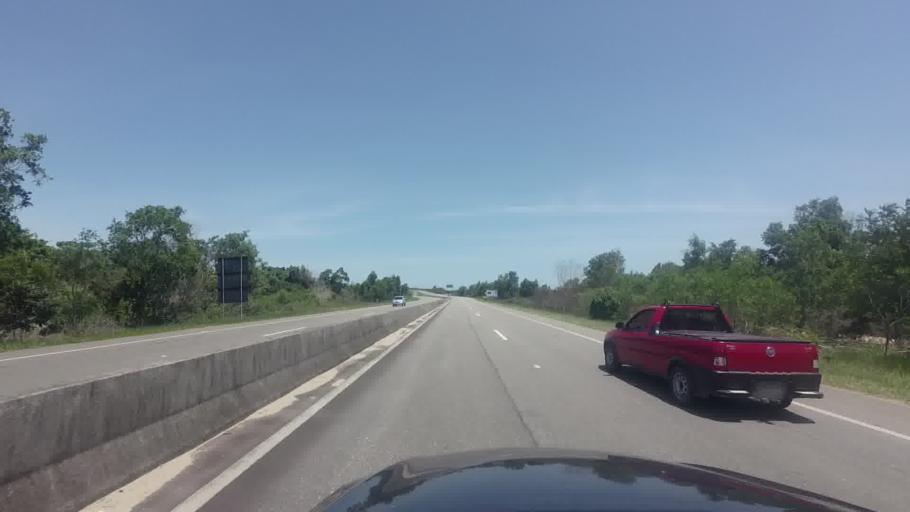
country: BR
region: Espirito Santo
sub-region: Guarapari
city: Guarapari
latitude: -20.6199
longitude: -40.4369
